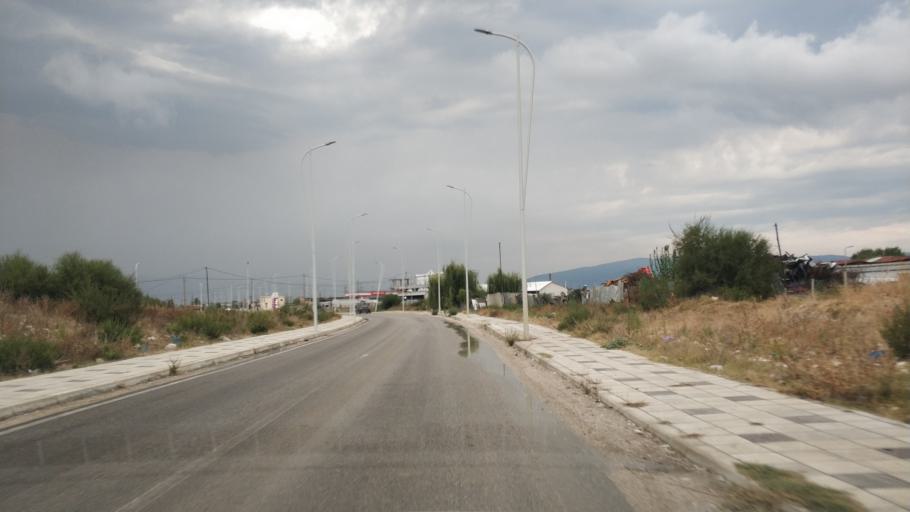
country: AL
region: Vlore
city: Vlore
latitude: 40.4831
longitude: 19.4669
